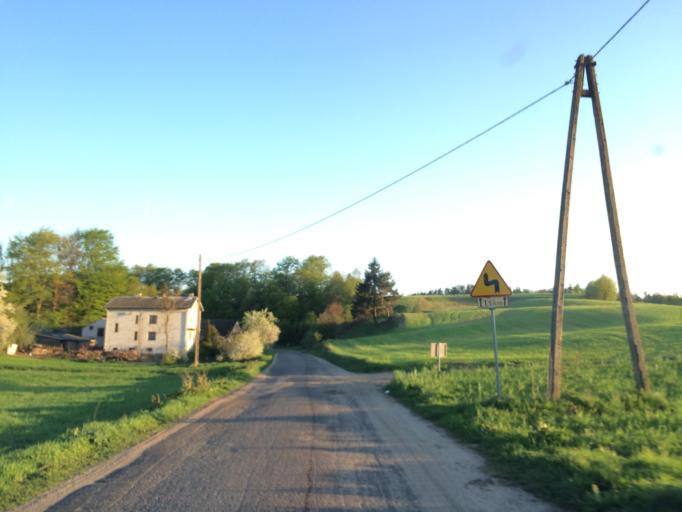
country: PL
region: Warmian-Masurian Voivodeship
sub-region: Powiat ilawski
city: Lubawa
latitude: 53.5249
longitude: 19.8750
